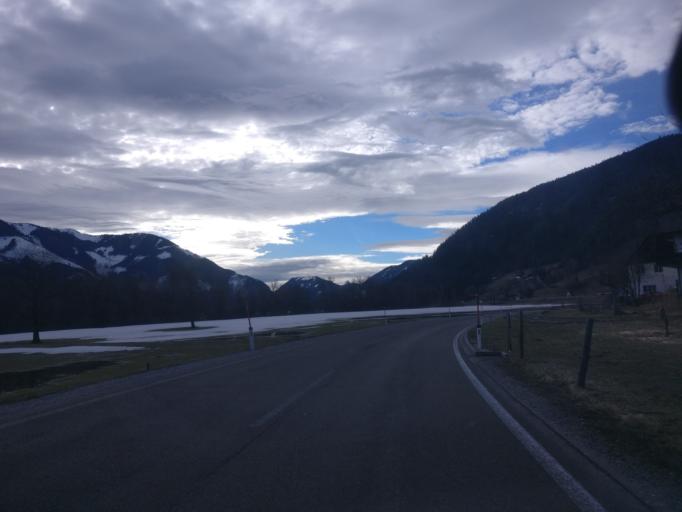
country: AT
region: Styria
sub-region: Politischer Bezirk Liezen
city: Admont
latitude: 47.5822
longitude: 14.4520
